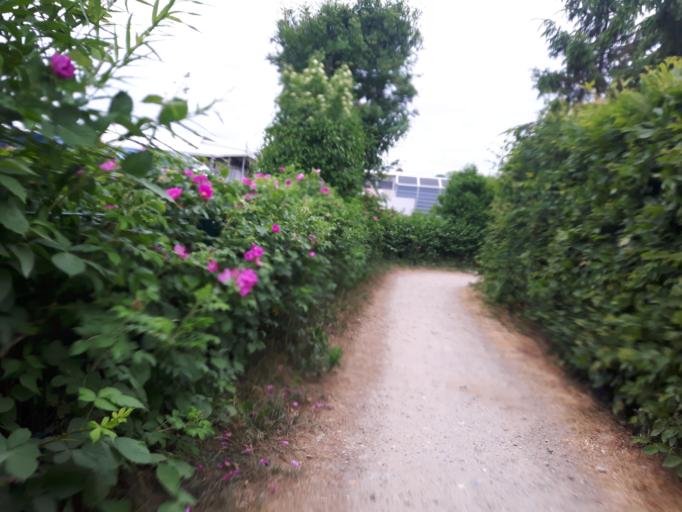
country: DE
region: Schleswig-Holstein
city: Schashagen
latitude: 54.0989
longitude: 10.8938
